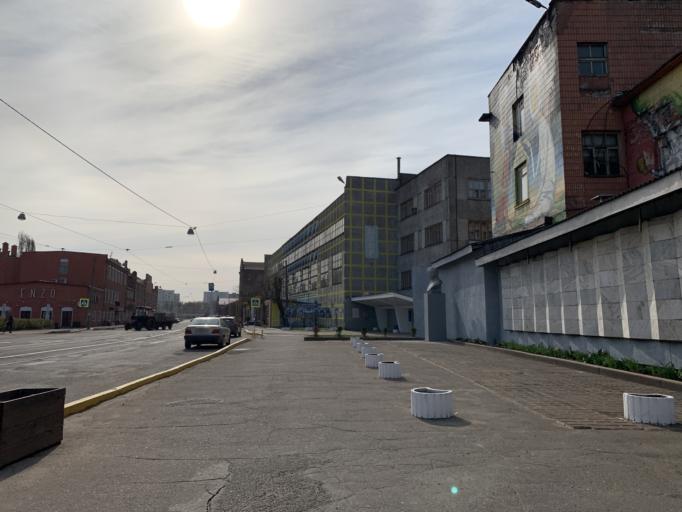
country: BY
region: Minsk
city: Minsk
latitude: 53.8902
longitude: 27.5732
